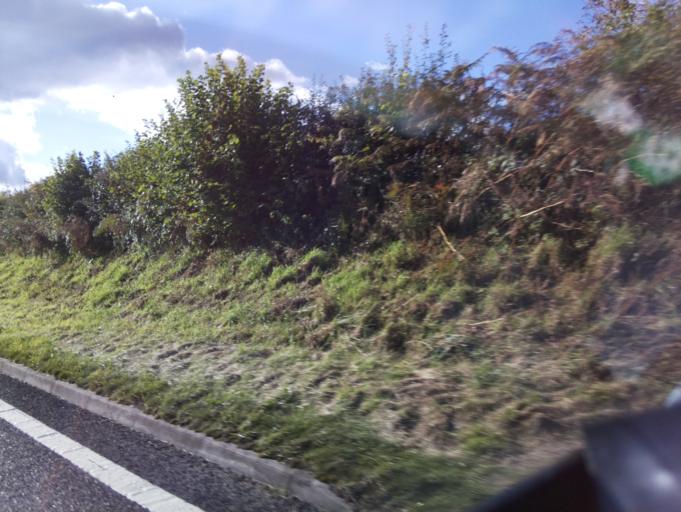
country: GB
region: Wales
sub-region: Sir Powys
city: Brecon
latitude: 51.9930
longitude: -3.3136
